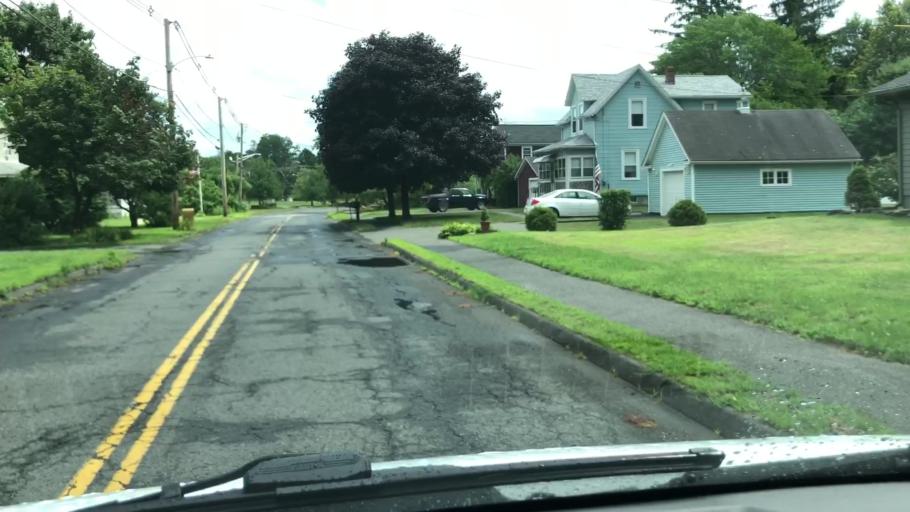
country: US
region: Massachusetts
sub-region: Hampshire County
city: Northampton
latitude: 42.3322
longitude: -72.6815
